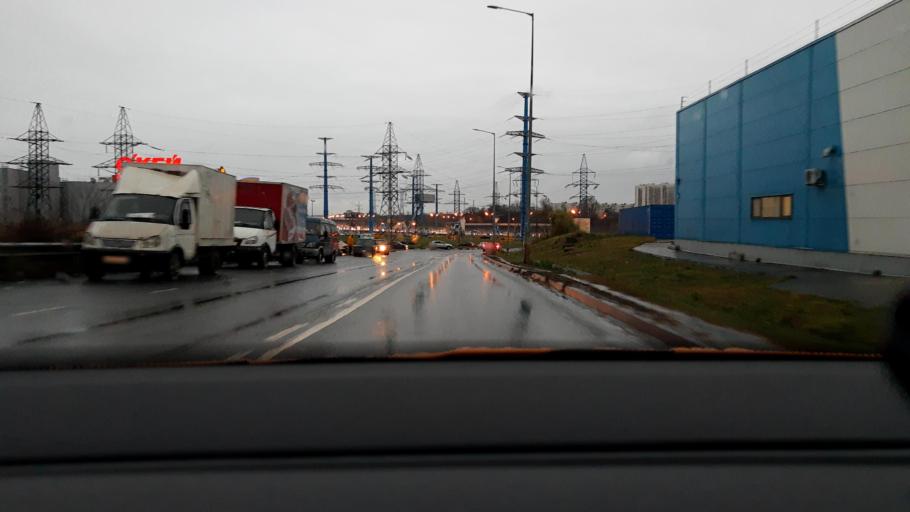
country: RU
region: Moscow
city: Lianozovo
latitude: 55.9137
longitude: 37.5779
